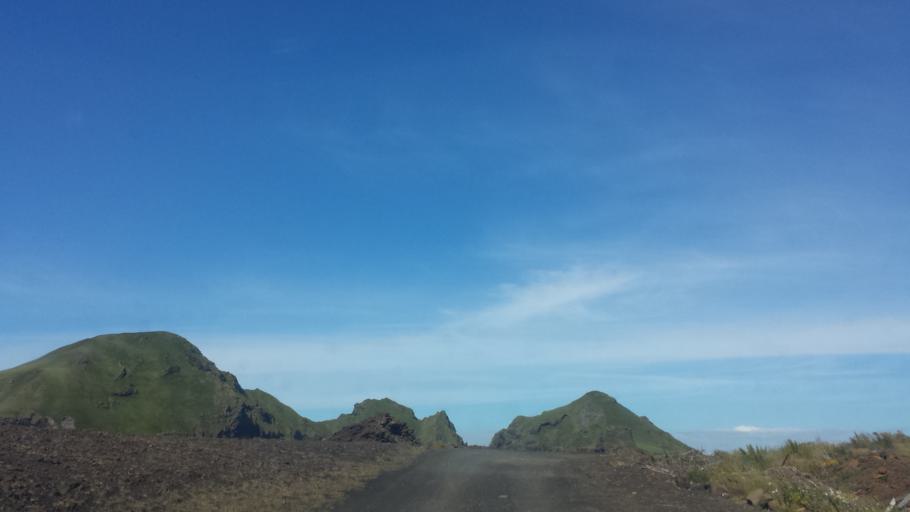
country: IS
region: South
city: Vestmannaeyjar
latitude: 63.4387
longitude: -20.2455
